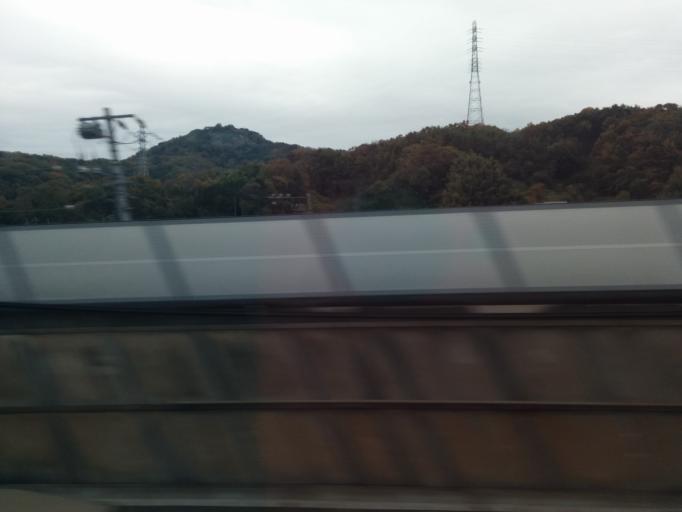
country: JP
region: Kanagawa
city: Oiso
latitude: 35.3228
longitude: 139.2862
